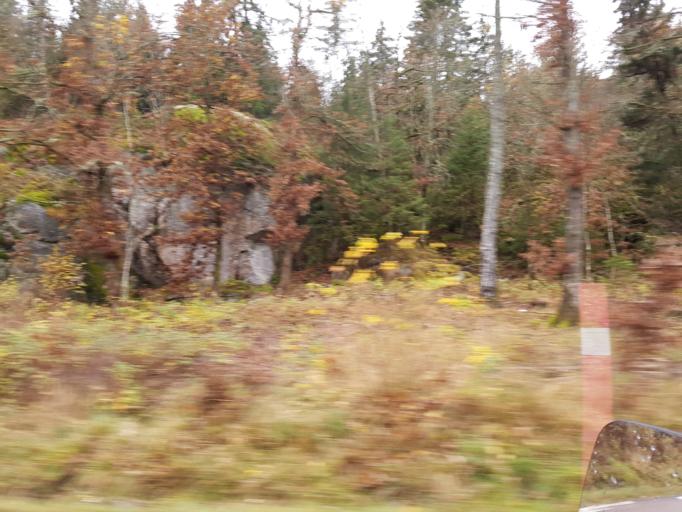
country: SE
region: Vaestra Goetaland
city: Svanesund
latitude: 58.1838
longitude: 11.8312
